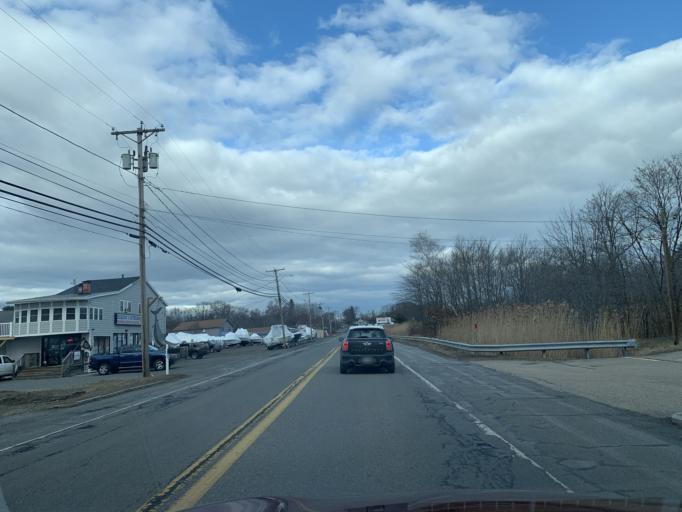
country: US
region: Massachusetts
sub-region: Essex County
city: Salisbury
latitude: 42.8343
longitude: -70.8620
